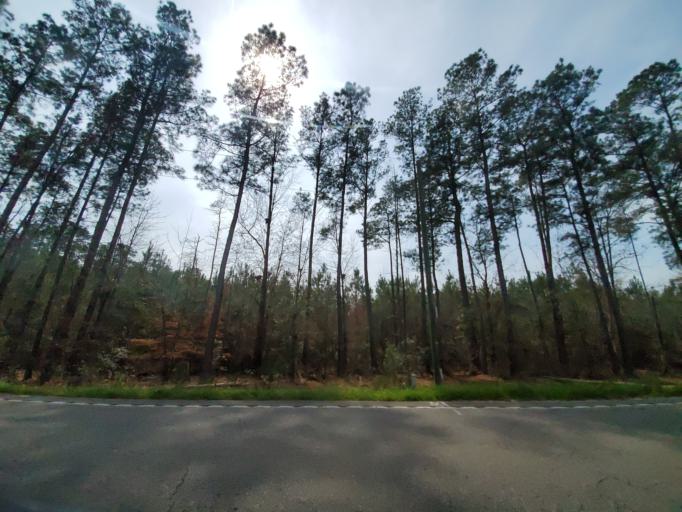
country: US
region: South Carolina
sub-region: Dorchester County
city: Ridgeville
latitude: 32.9699
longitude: -80.3043
